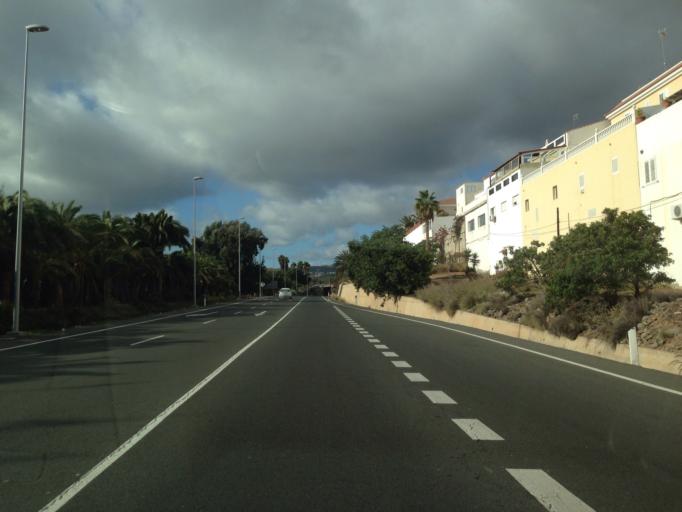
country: ES
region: Canary Islands
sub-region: Provincia de Las Palmas
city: Maspalomas
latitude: 27.7645
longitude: -15.5881
